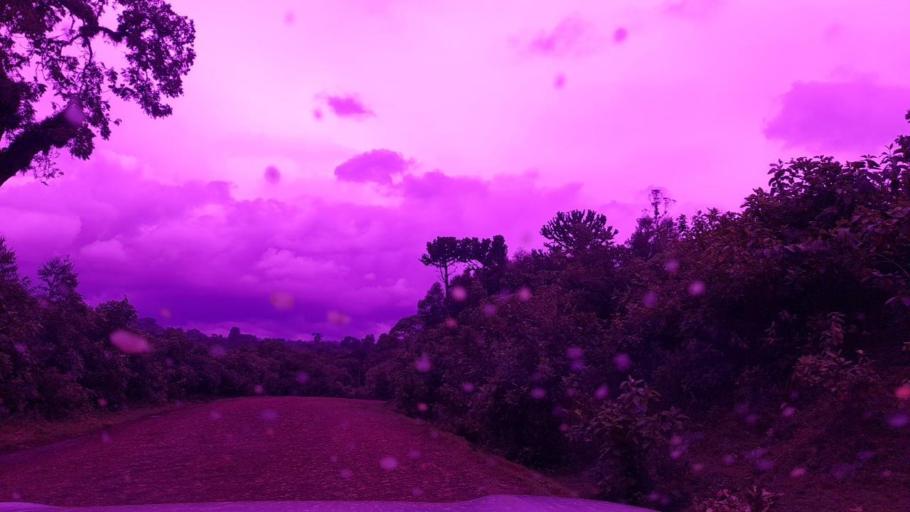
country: ET
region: Southern Nations, Nationalities, and People's Region
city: Tippi
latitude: 7.5792
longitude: 35.6652
